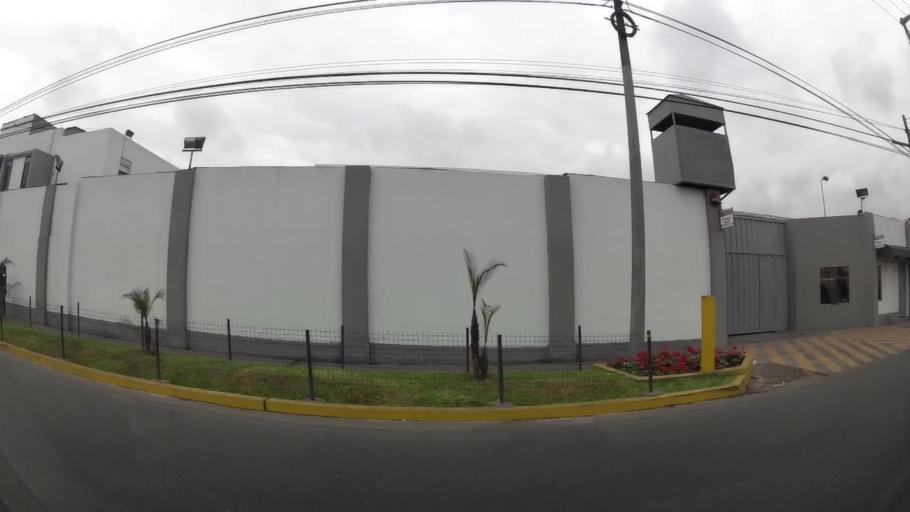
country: PE
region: Lima
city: Lima
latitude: -12.0461
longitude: -77.0725
